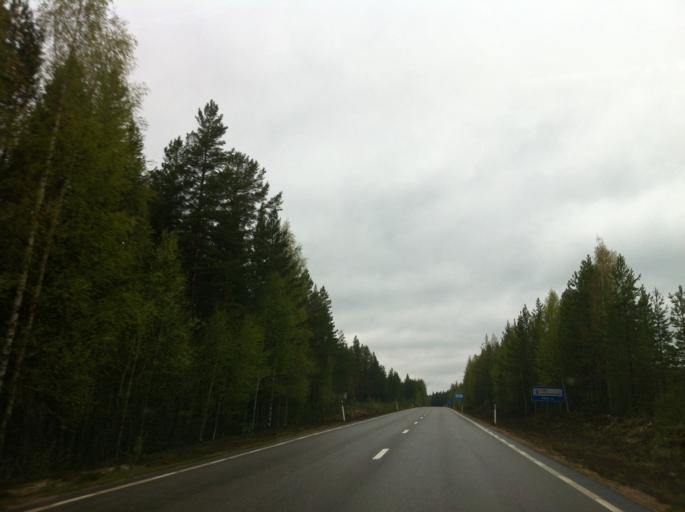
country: SE
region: Jaemtland
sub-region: Harjedalens Kommun
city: Sveg
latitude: 62.1150
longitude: 14.1775
